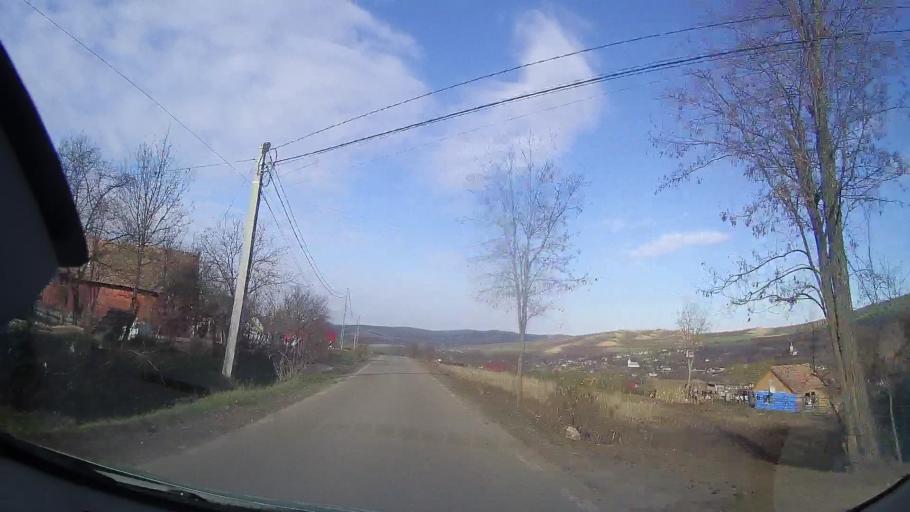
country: RO
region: Mures
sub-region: Comuna Sanger
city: Sanger
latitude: 46.5509
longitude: 24.1447
